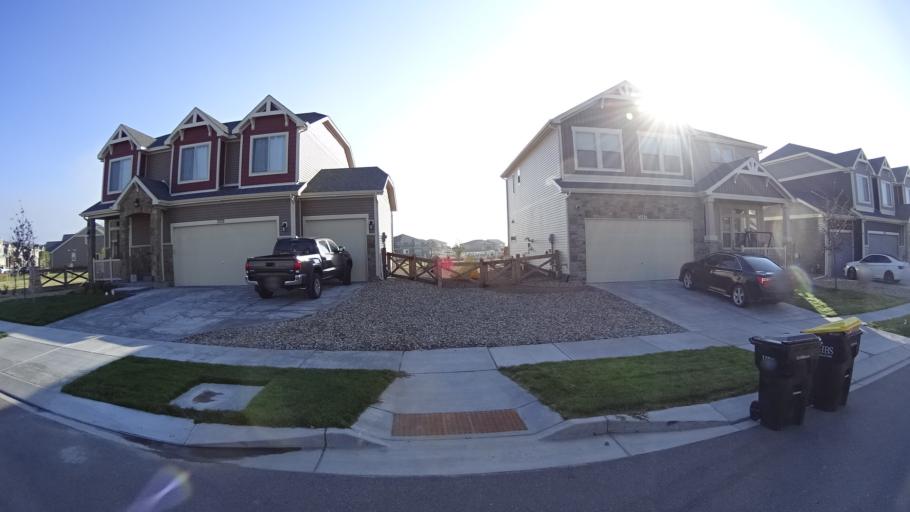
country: US
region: Colorado
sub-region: El Paso County
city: Cimarron Hills
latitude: 38.9328
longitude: -104.6563
